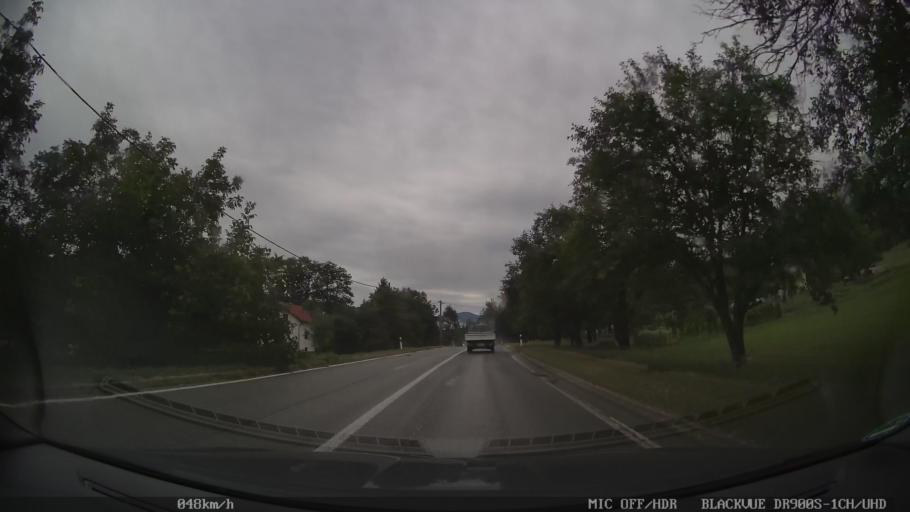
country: HR
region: Licko-Senjska
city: Jezerce
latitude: 44.7688
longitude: 15.6677
